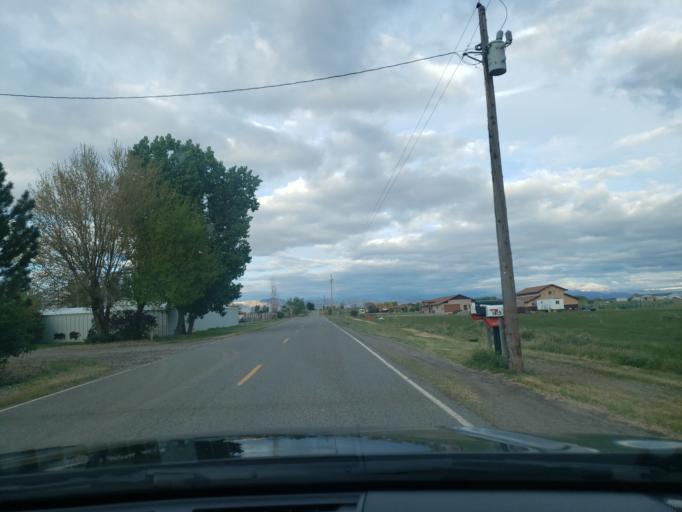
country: US
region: Colorado
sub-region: Mesa County
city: Fruita
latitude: 39.2221
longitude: -108.7174
